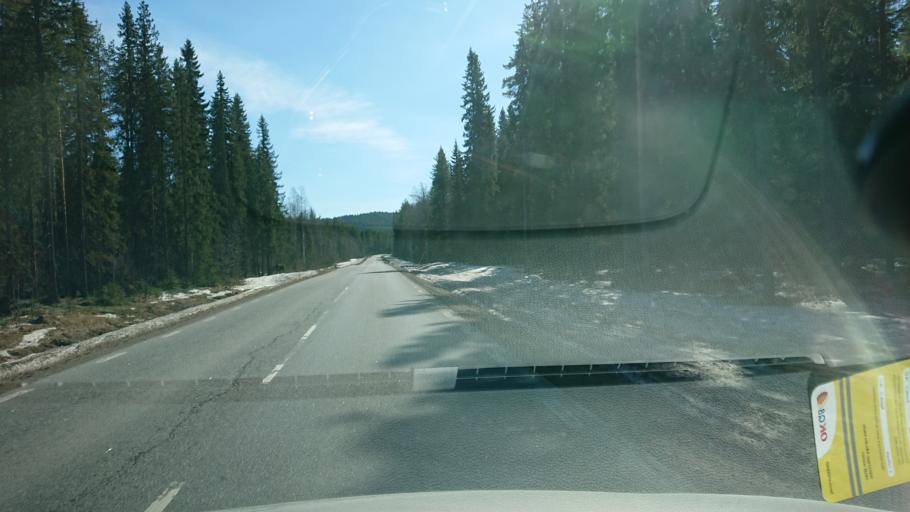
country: SE
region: Vaesternorrland
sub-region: Solleftea Kommun
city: As
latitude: 63.5723
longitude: 16.4471
